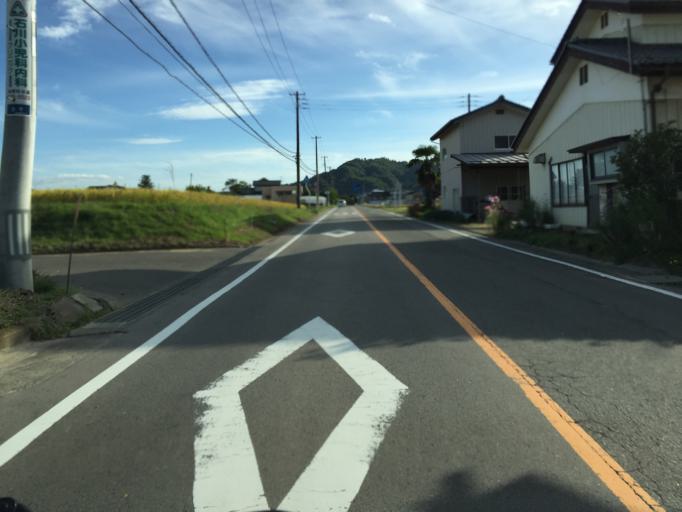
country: JP
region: Fukushima
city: Yanagawamachi-saiwaicho
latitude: 37.8140
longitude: 140.6194
